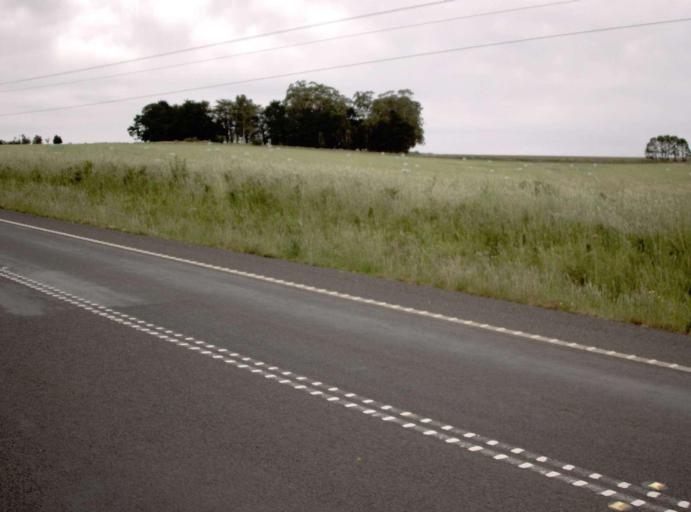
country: AU
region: Victoria
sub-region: Baw Baw
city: Warragul
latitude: -38.4570
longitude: 145.9292
